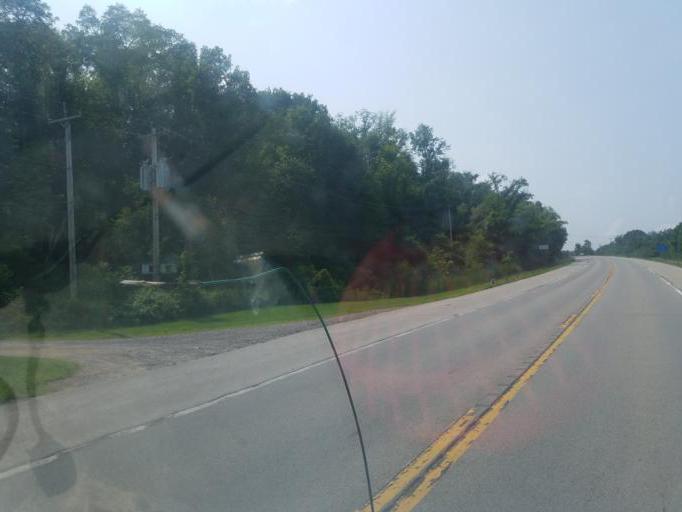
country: US
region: New York
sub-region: Montgomery County
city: Tribes Hill
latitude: 42.9345
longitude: -74.3299
